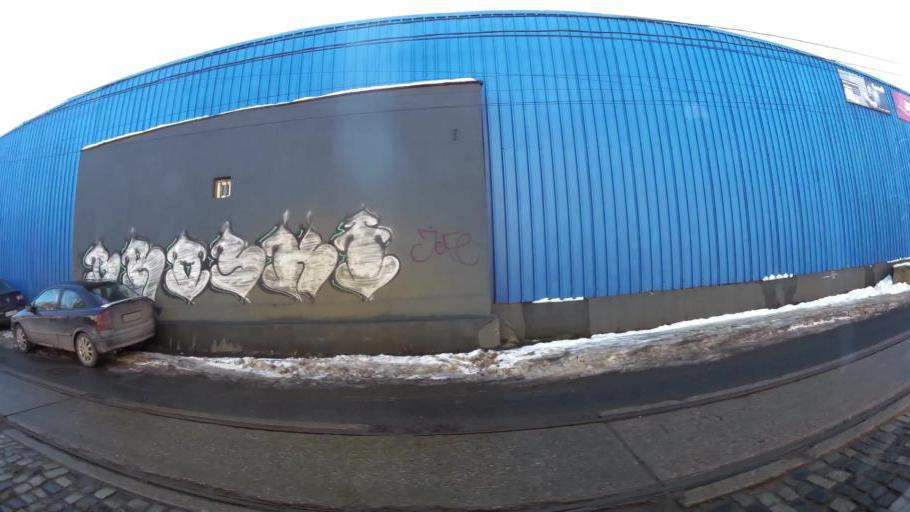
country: RO
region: Bucuresti
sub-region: Municipiul Bucuresti
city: Bucharest
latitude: 44.4547
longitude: 26.1227
